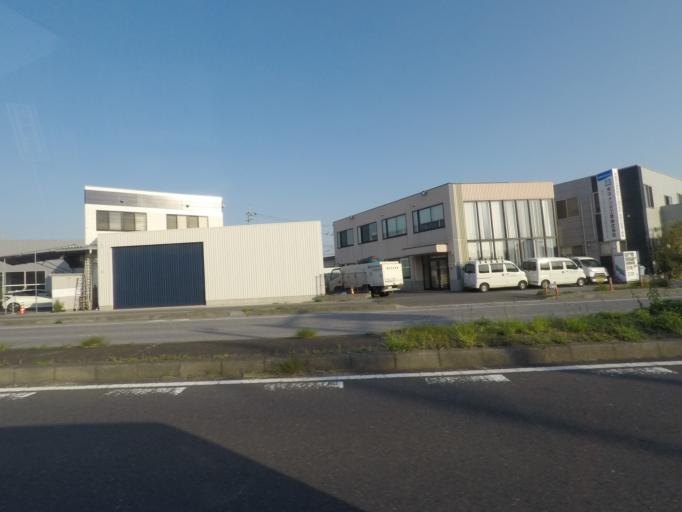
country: JP
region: Chiba
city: Yotsukaido
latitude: 35.6300
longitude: 140.1558
